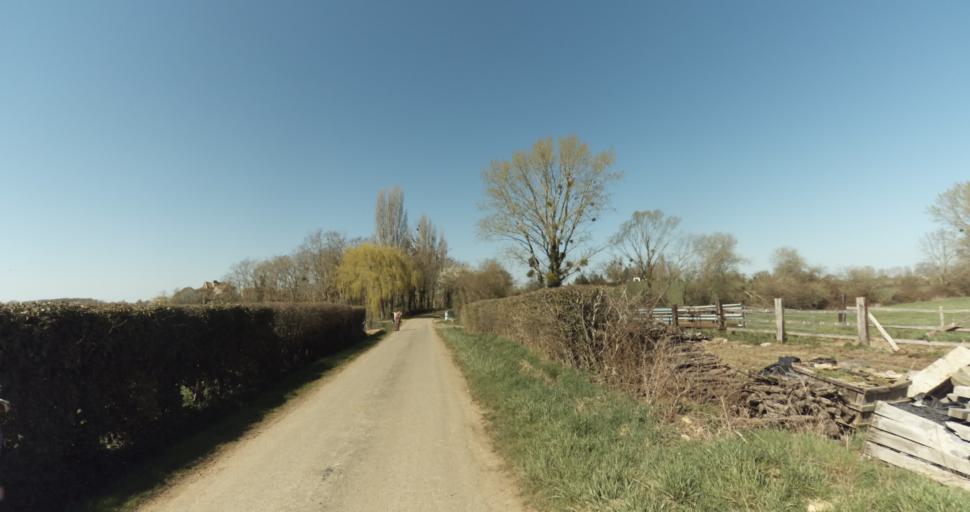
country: FR
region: Lower Normandy
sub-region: Departement du Calvados
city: Saint-Pierre-sur-Dives
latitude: 49.0074
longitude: 0.0180
